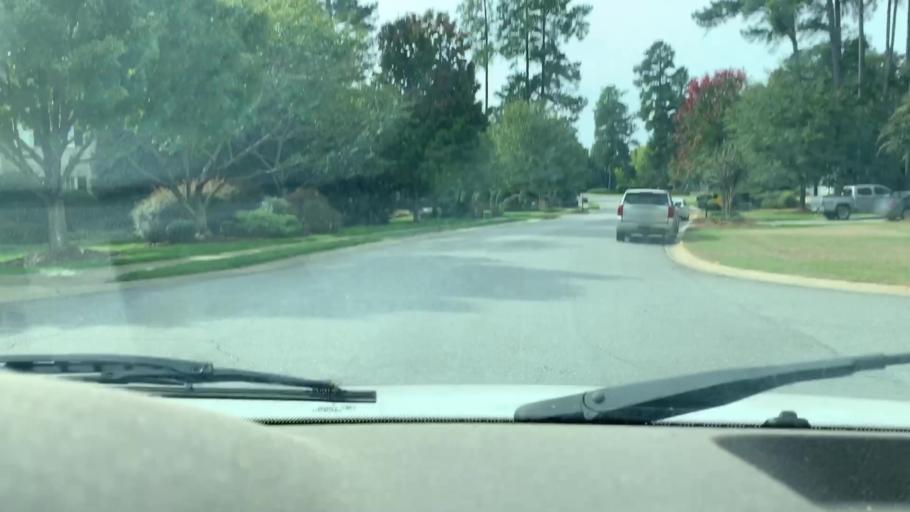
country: US
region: North Carolina
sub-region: Lincoln County
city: Westport
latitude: 35.4690
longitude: -80.9304
